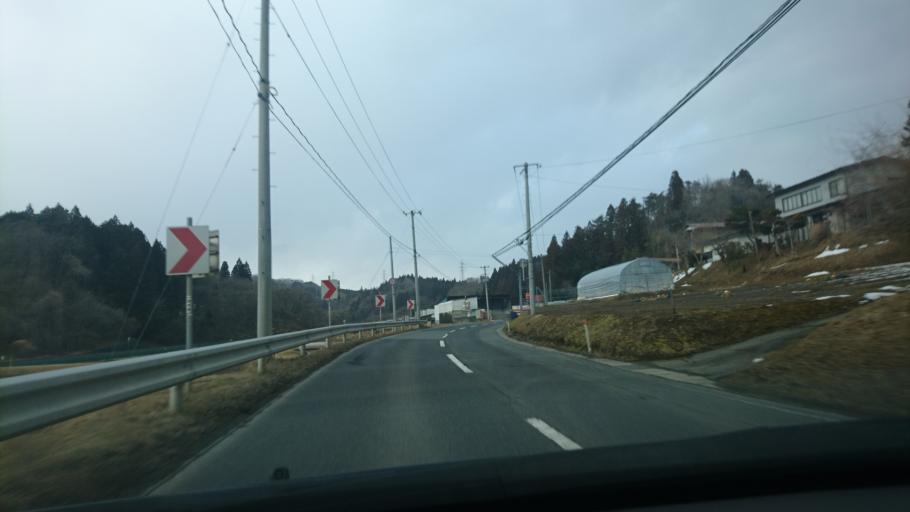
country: JP
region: Iwate
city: Ichinoseki
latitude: 38.9498
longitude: 141.3365
